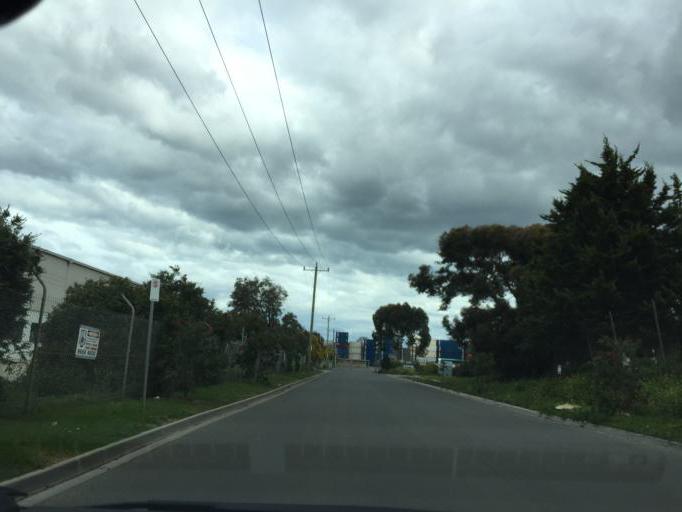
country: AU
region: Victoria
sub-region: Maribyrnong
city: Braybrook
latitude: -37.8030
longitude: 144.8573
